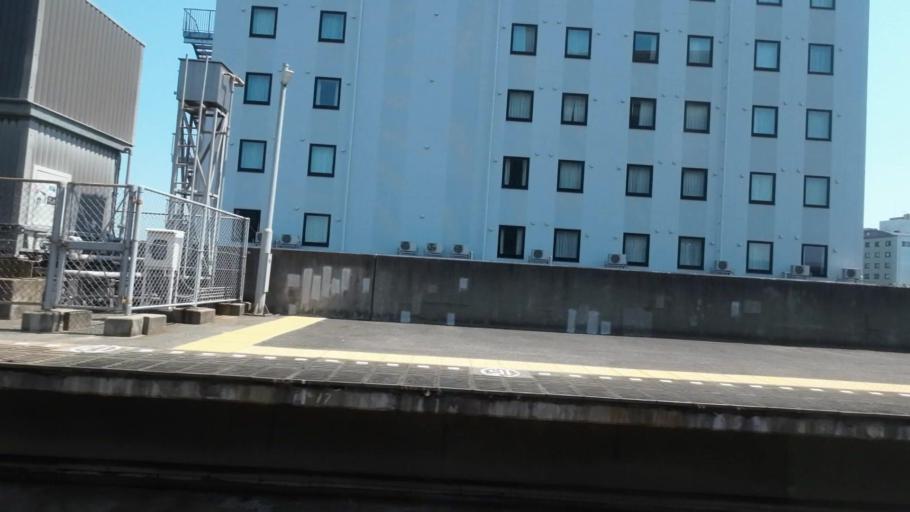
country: JP
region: Ehime
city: Hojo
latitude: 34.0650
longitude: 132.9931
